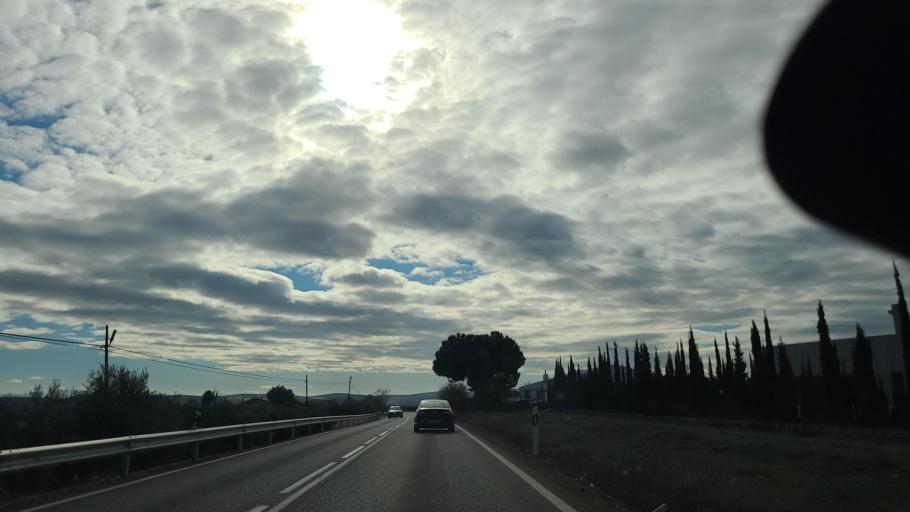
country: ES
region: Andalusia
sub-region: Provincia de Jaen
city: Villanueva de la Reina
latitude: 38.0399
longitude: -3.9146
